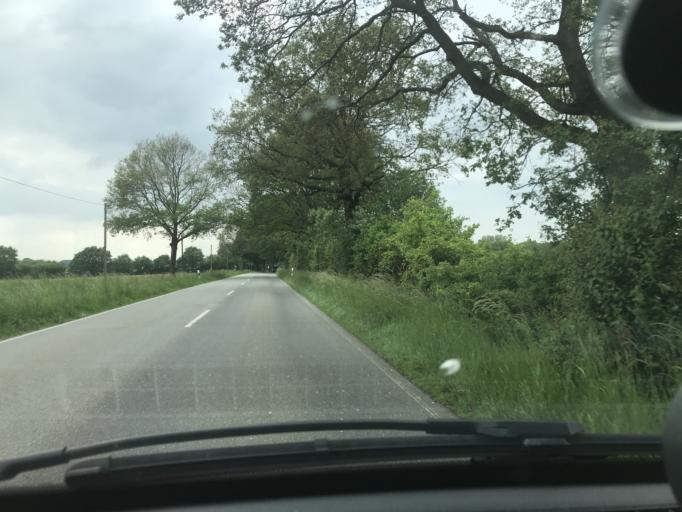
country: DE
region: Schleswig-Holstein
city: Siek
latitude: 53.6127
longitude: 10.3111
